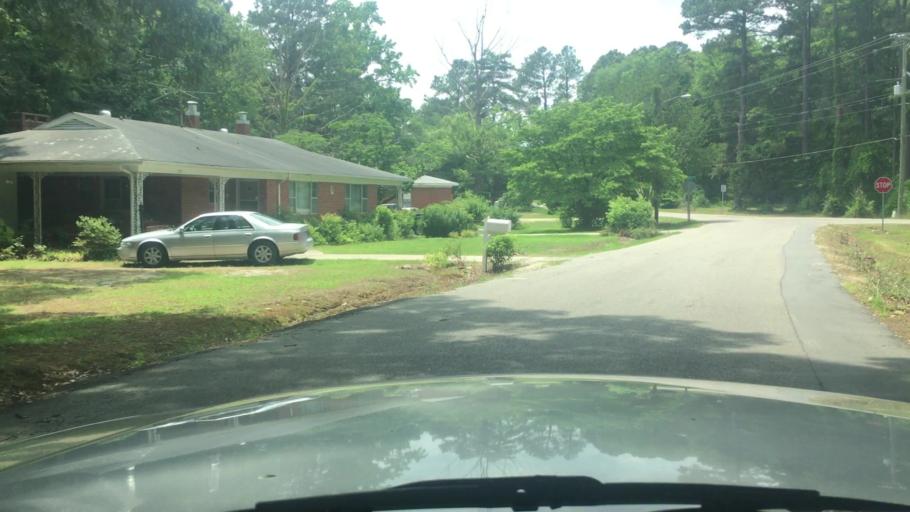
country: US
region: North Carolina
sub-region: Cumberland County
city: Fort Bragg
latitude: 35.0900
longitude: -78.9586
